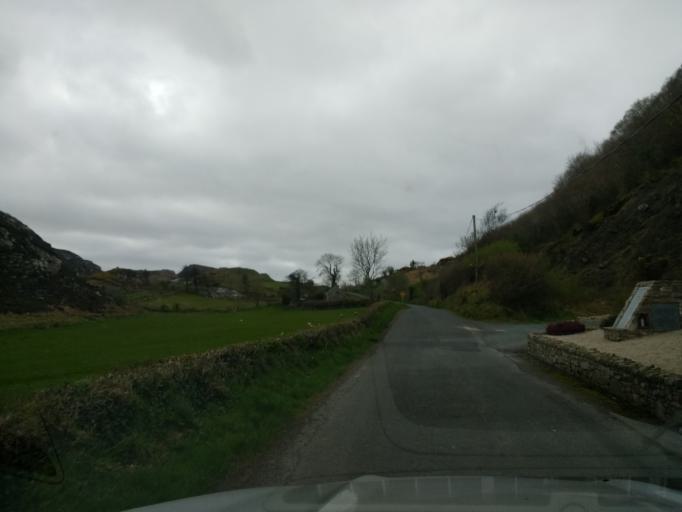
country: IE
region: Ulster
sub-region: County Donegal
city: Ramelton
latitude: 55.2267
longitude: -7.6226
